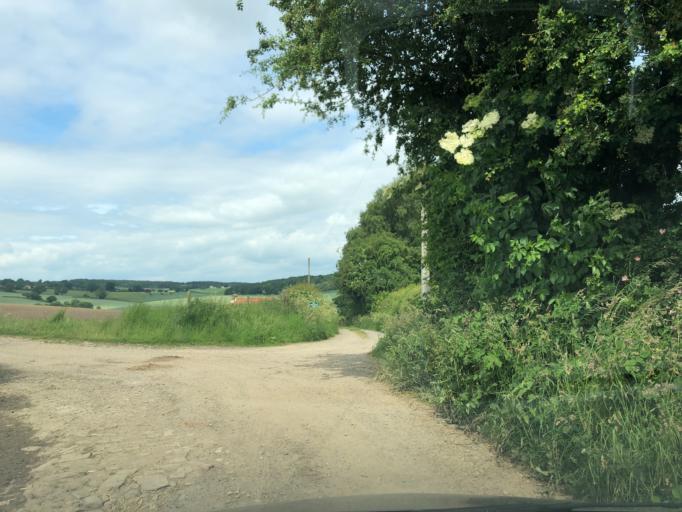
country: GB
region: England
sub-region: North Yorkshire
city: Helmsley
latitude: 54.1592
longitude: -1.0063
